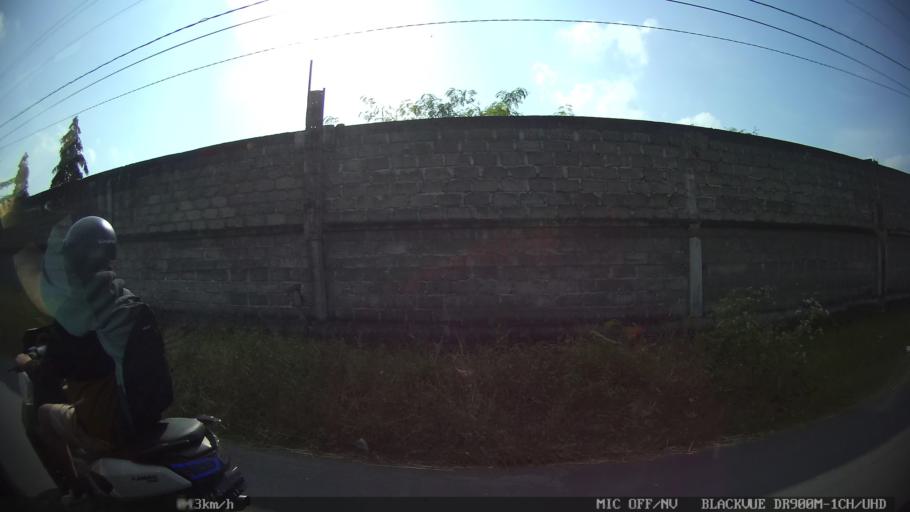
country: ID
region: Daerah Istimewa Yogyakarta
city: Gamping Lor
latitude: -7.8100
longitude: 110.2996
